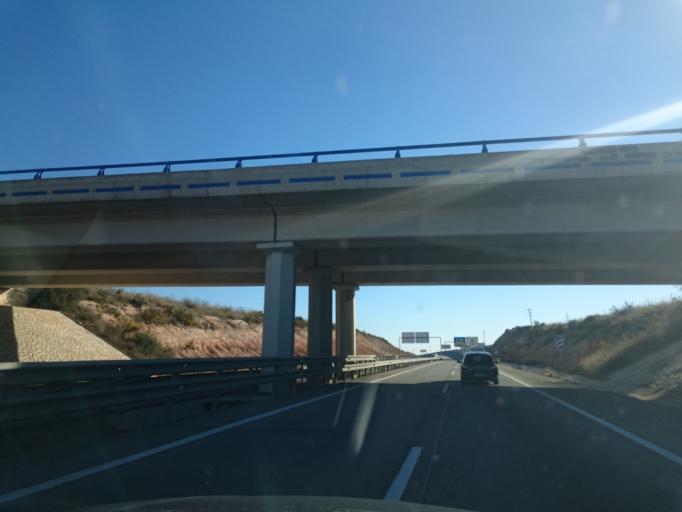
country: ES
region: Catalonia
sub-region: Provincia de Tarragona
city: Constanti
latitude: 41.1266
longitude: 1.1879
